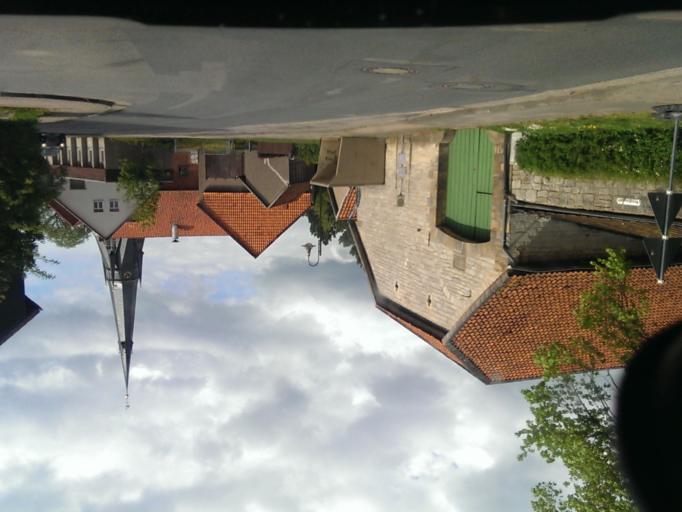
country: DE
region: Lower Saxony
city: Eime
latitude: 52.0781
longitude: 9.7231
